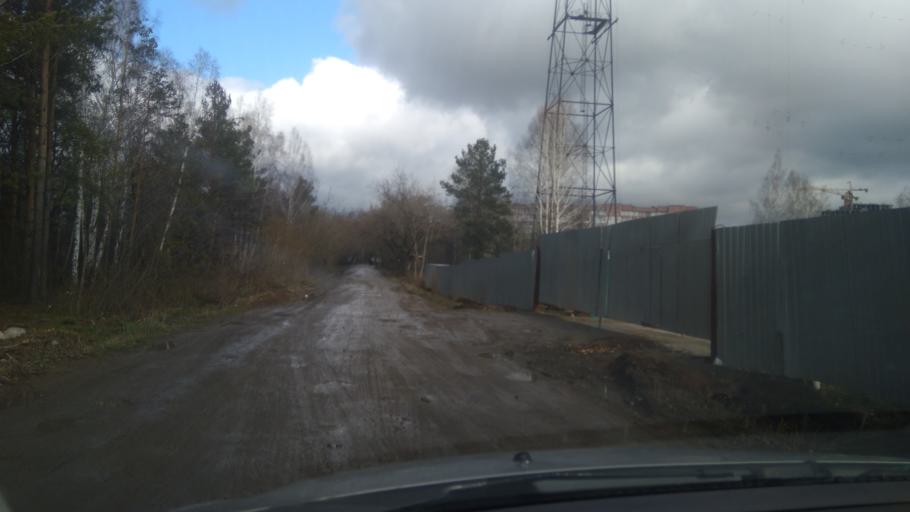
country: RU
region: Sverdlovsk
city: Verkhnyaya Pyshma
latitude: 56.9236
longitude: 60.6052
